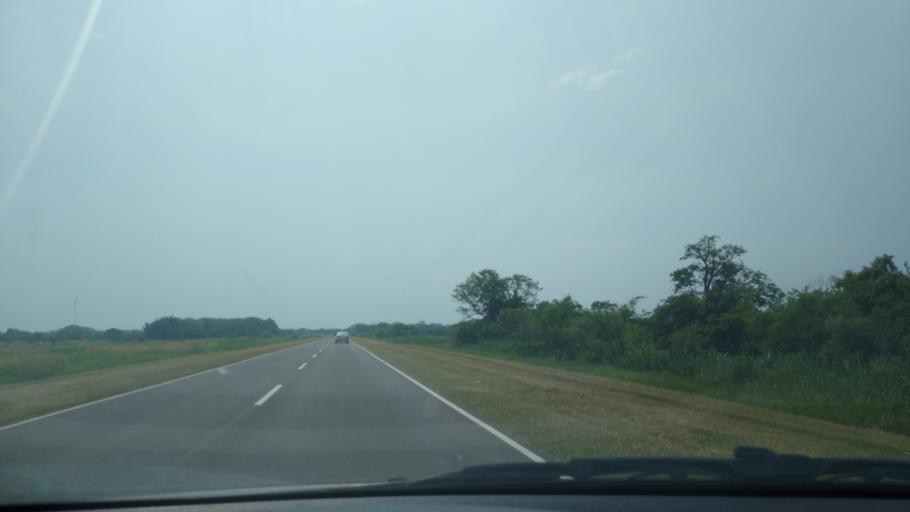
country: AR
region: Chaco
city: La Eduvigis
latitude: -26.8470
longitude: -59.0502
